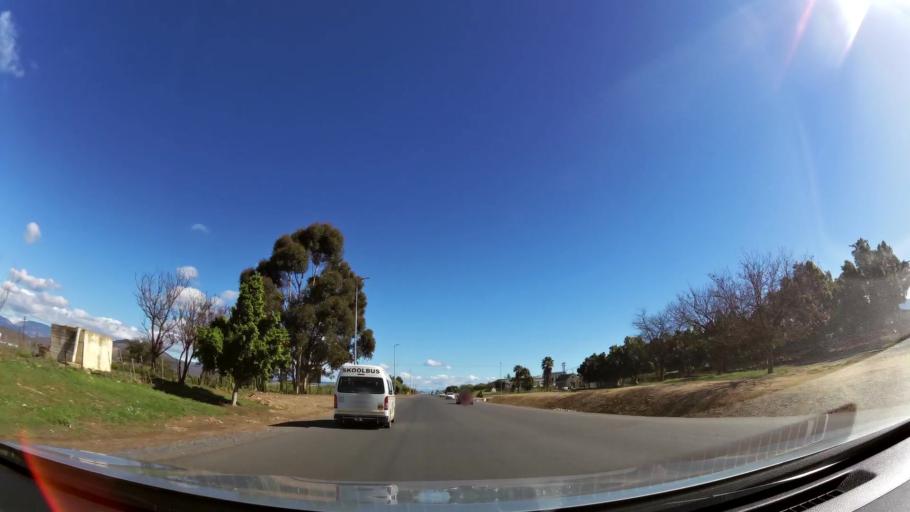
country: ZA
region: Western Cape
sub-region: Cape Winelands District Municipality
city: Ashton
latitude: -33.8370
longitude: 20.0372
